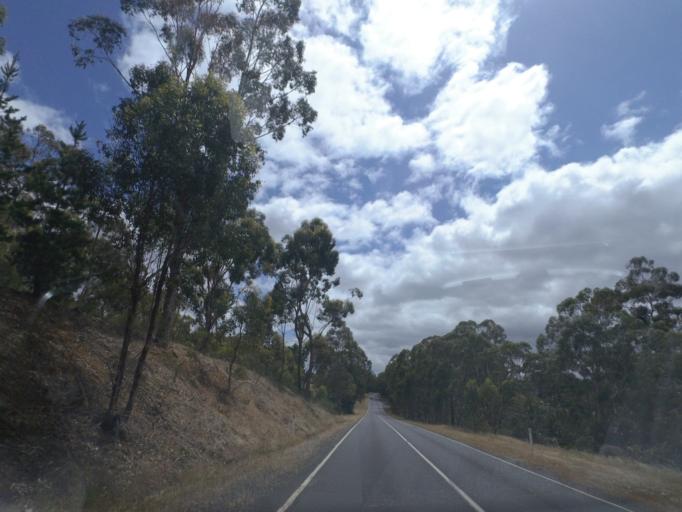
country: AU
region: Victoria
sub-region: Whittlesea
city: Whittlesea
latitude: -37.2329
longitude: 145.0469
